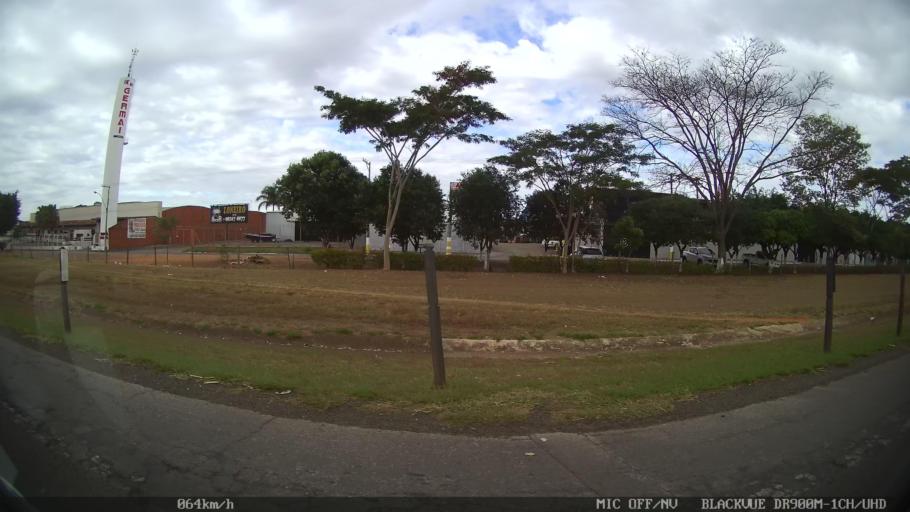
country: BR
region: Sao Paulo
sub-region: Bady Bassitt
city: Bady Bassitt
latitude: -20.8060
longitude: -49.5207
